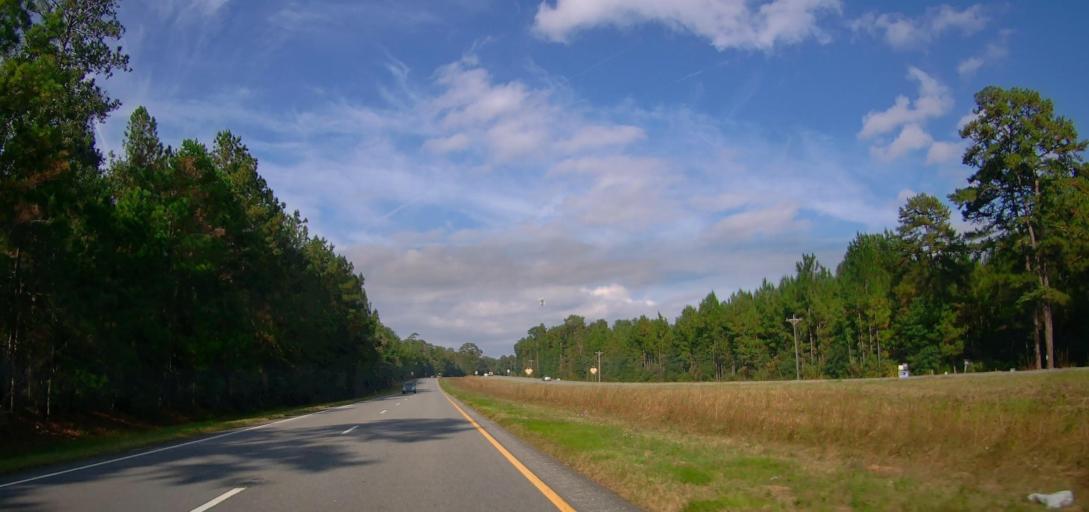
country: US
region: Georgia
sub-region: Grady County
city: Cairo
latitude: 30.7034
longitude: -84.1459
